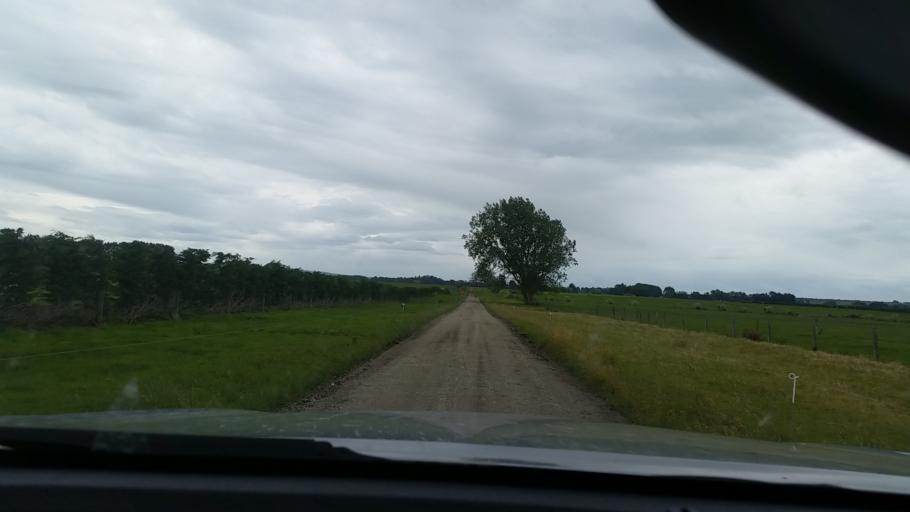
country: NZ
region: Southland
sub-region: Gore District
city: Gore
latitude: -46.2721
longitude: 168.7661
